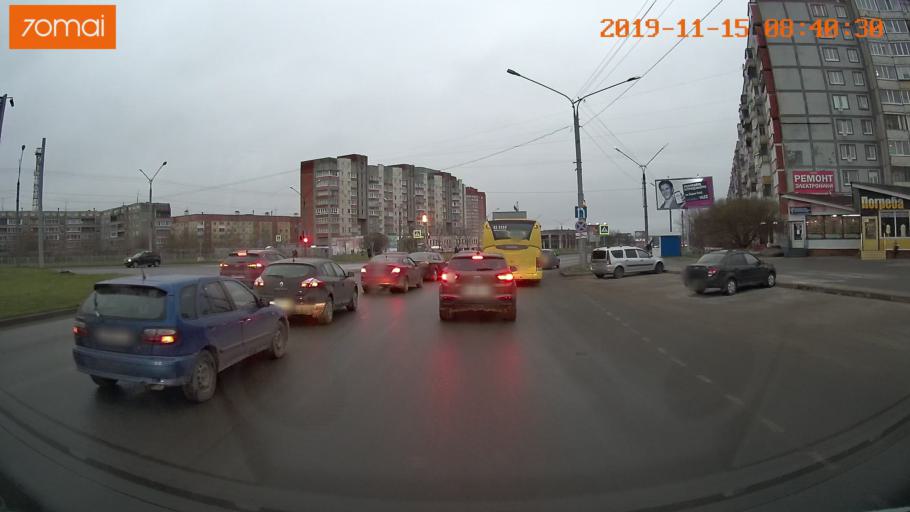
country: RU
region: Vologda
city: Cherepovets
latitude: 59.0948
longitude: 37.9142
